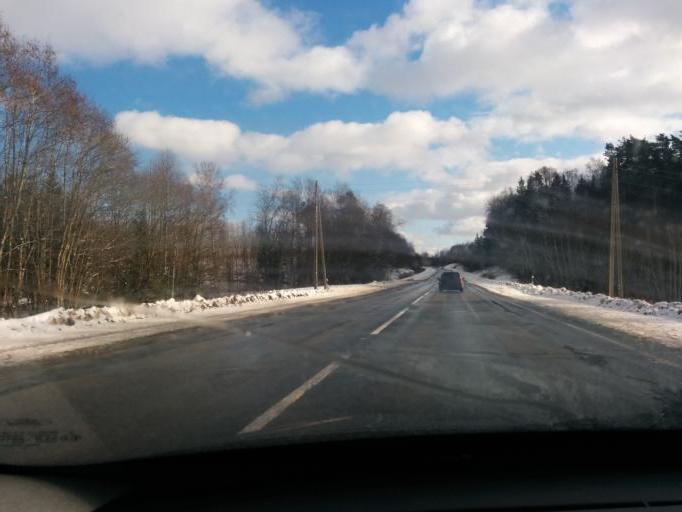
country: LV
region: Raunas
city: Rauna
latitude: 57.3178
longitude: 25.7125
